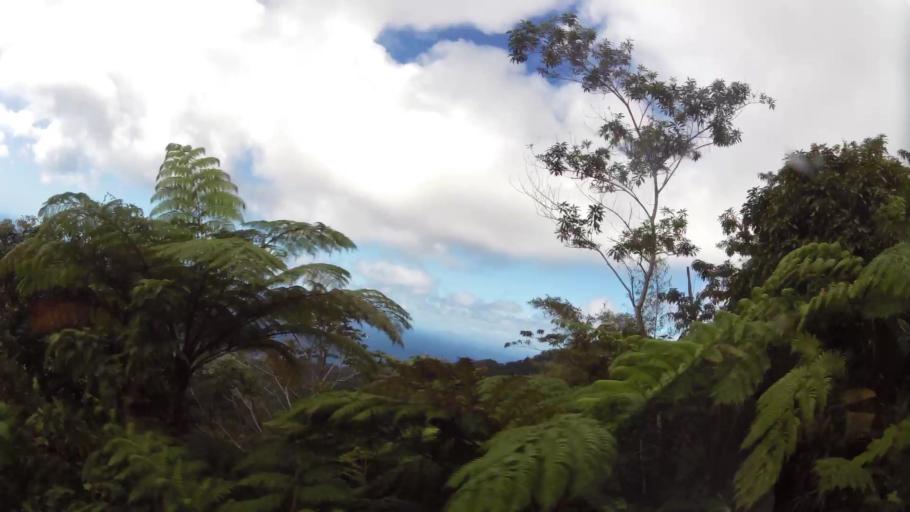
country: DM
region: Saint John
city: Portsmouth
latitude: 15.6149
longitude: -61.4447
